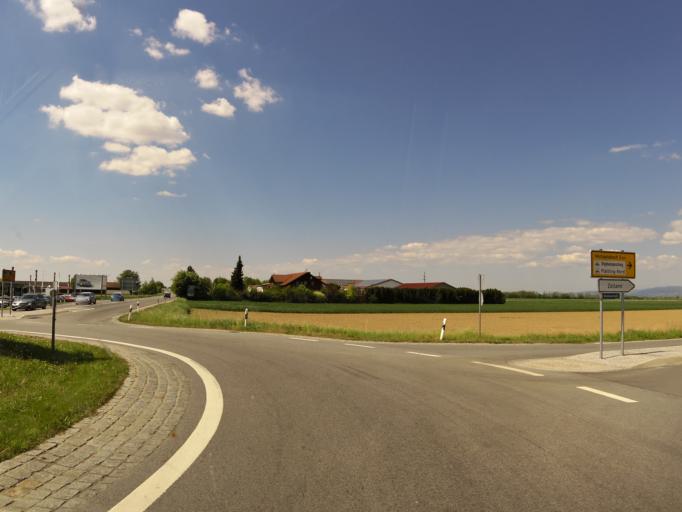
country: DE
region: Bavaria
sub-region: Lower Bavaria
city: Plattling
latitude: 48.7871
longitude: 12.8501
